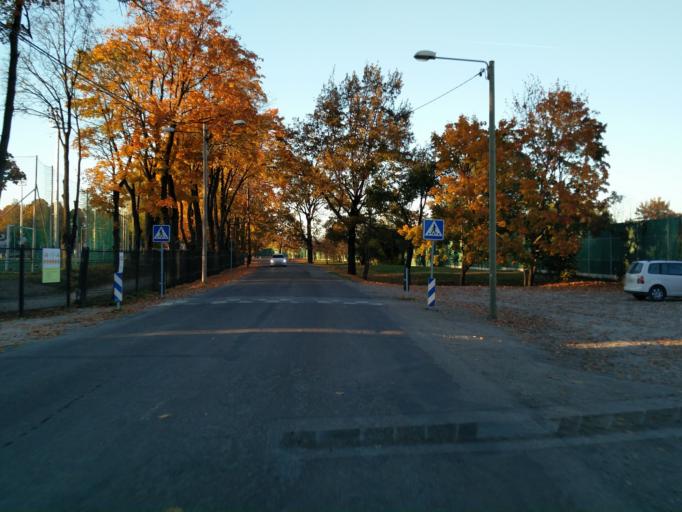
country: EE
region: Tartu
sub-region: Tartu linn
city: Tartu
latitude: 58.3650
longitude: 26.7166
